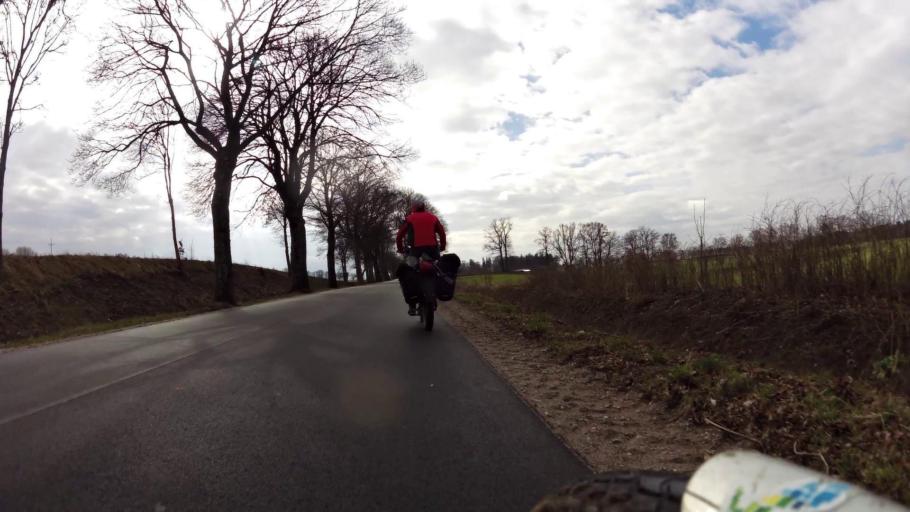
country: PL
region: Pomeranian Voivodeship
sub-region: Powiat bytowski
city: Kolczyglowy
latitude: 54.2256
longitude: 17.2409
